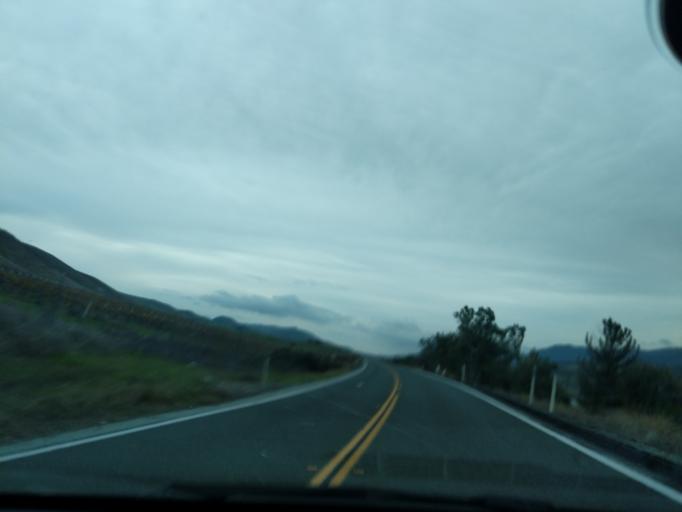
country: US
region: California
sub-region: San Benito County
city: Ridgemark
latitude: 36.7015
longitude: -121.2748
